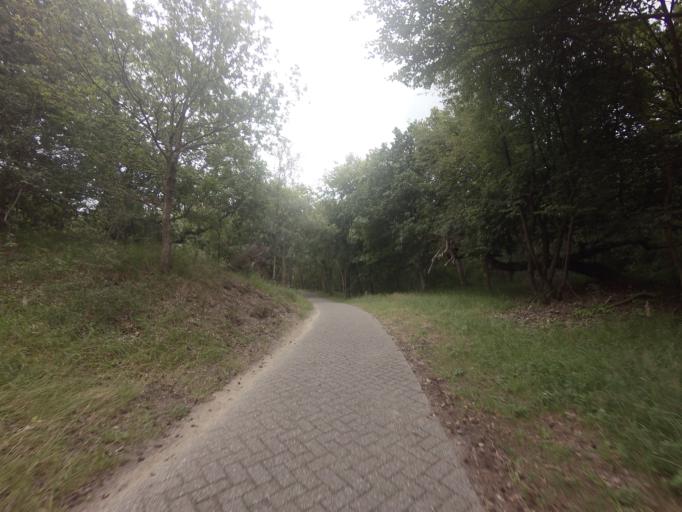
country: NL
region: North Holland
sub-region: Gemeente Bloemendaal
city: Bloemendaal
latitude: 52.4205
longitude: 4.6086
